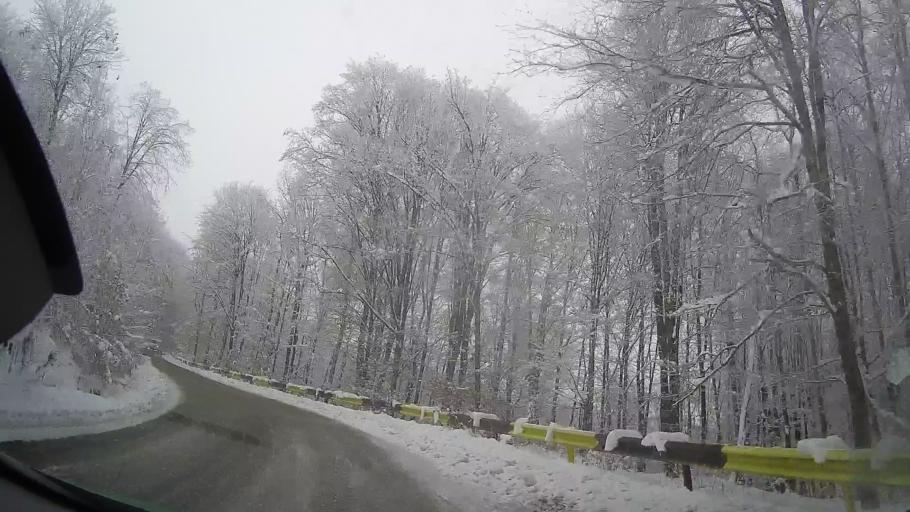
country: RO
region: Neamt
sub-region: Comuna Valea Ursului
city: Valea Ursului
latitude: 46.8430
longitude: 27.0677
